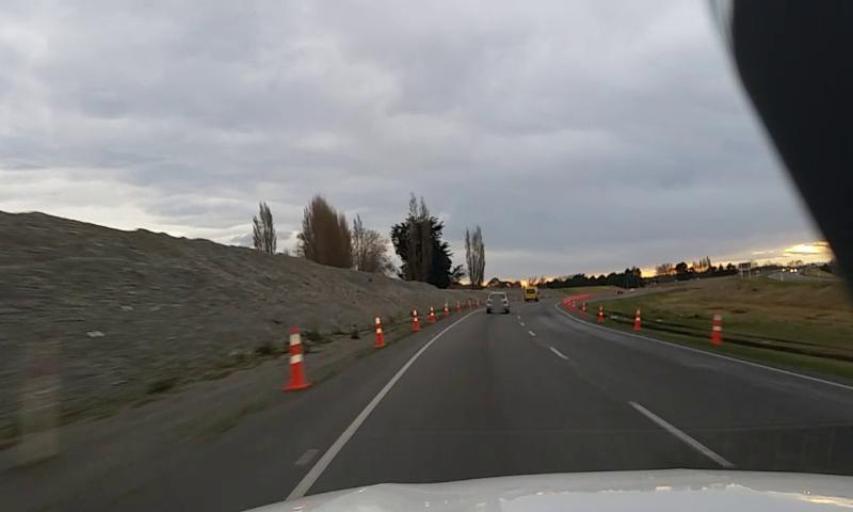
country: NZ
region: Canterbury
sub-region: Waimakariri District
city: Kaiapoi
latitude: -43.4331
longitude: 172.6404
